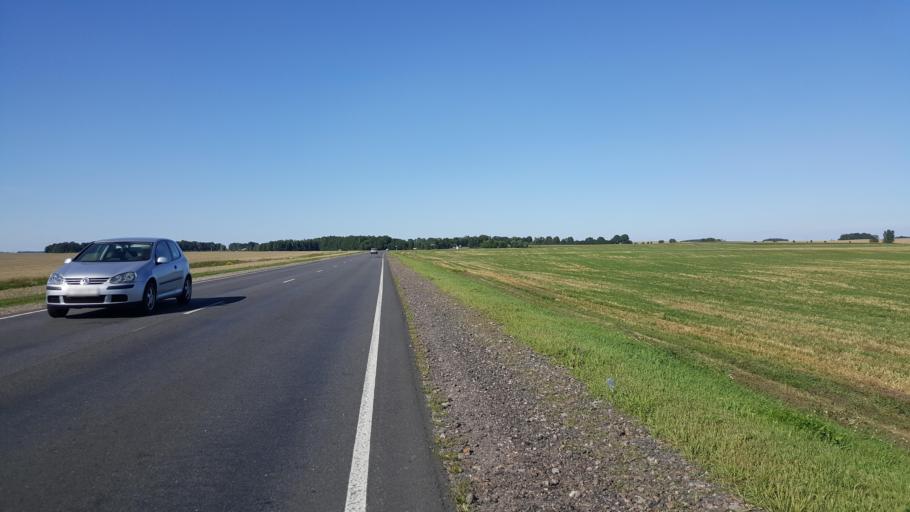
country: BY
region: Brest
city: Charnawchytsy
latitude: 52.2526
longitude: 23.7532
